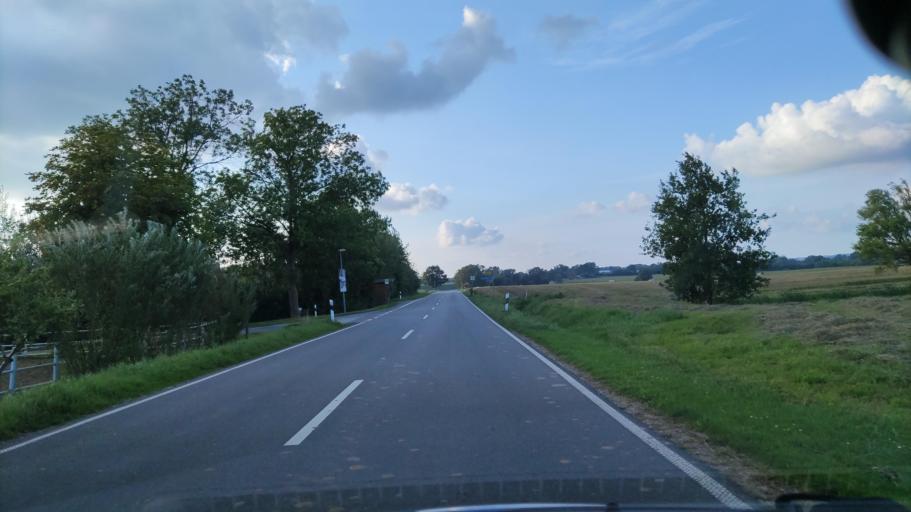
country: DE
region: Schleswig-Holstein
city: Glasau
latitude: 54.0397
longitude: 10.5386
